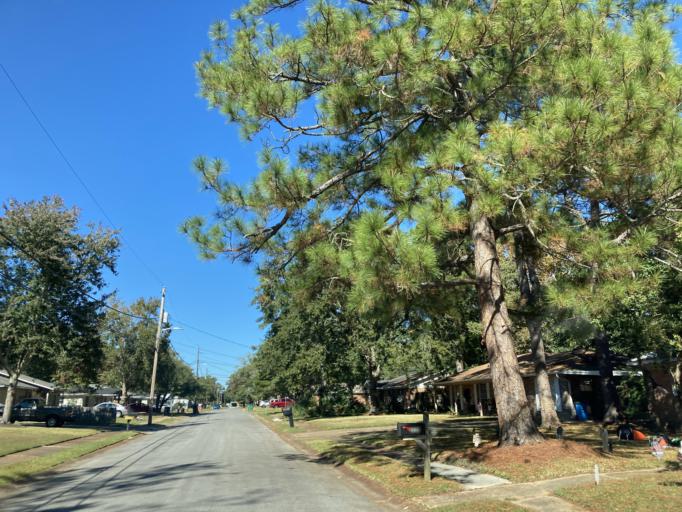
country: US
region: Mississippi
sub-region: Jackson County
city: Ocean Springs
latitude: 30.4041
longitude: -88.8091
